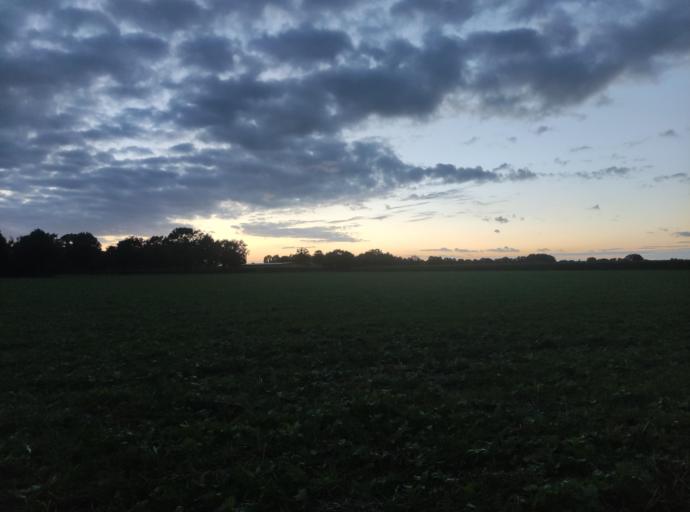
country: DE
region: North Rhine-Westphalia
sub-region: Regierungsbezirk Detmold
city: Rheda-Wiedenbruck
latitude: 51.8697
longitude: 8.2966
